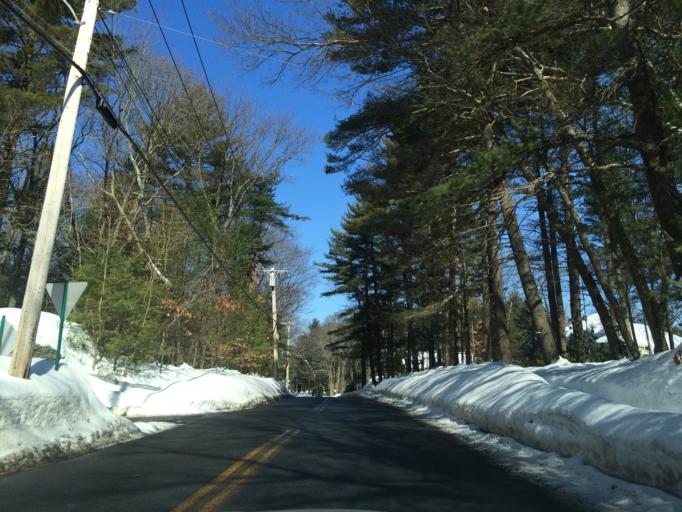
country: US
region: Massachusetts
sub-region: Norfolk County
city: Wellesley
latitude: 42.2816
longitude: -71.2883
